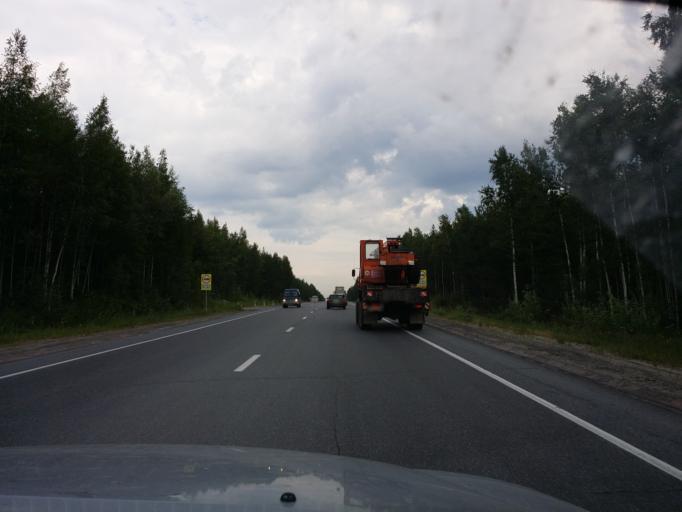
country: RU
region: Khanty-Mansiyskiy Avtonomnyy Okrug
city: Megion
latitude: 61.0546
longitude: 76.3087
